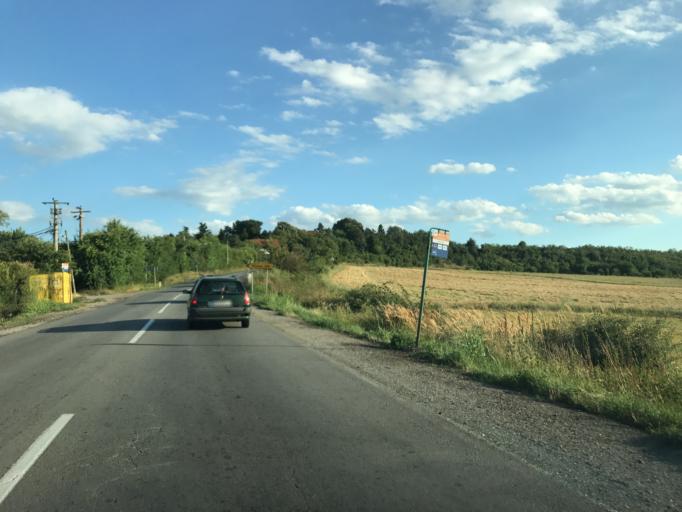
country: RS
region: Central Serbia
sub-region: Belgrade
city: Grocka
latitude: 44.7062
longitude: 20.6632
